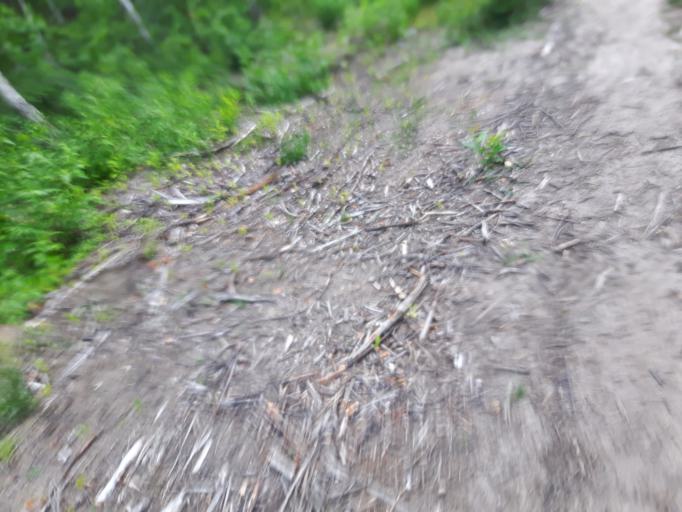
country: PL
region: Masovian Voivodeship
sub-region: Warszawa
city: Rembertow
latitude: 52.2778
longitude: 21.1371
